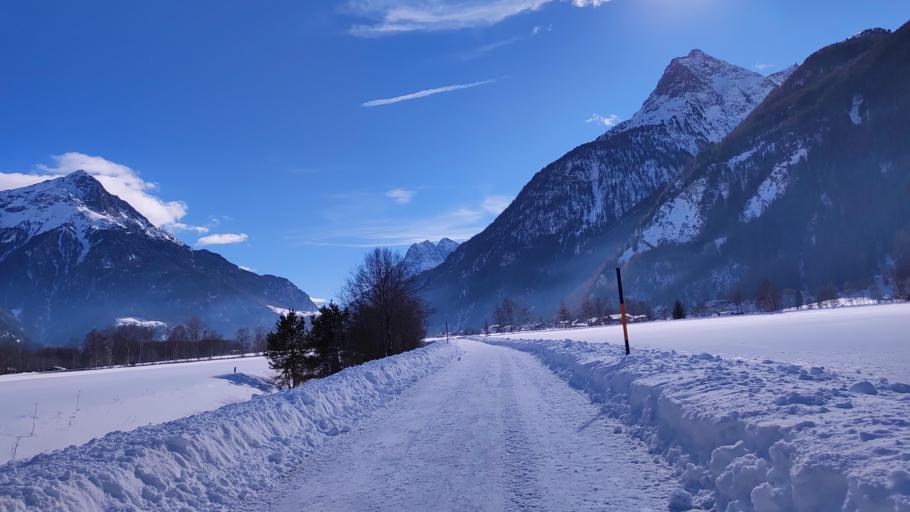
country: AT
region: Tyrol
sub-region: Politischer Bezirk Imst
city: Umhausen
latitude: 47.0976
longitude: 10.9426
